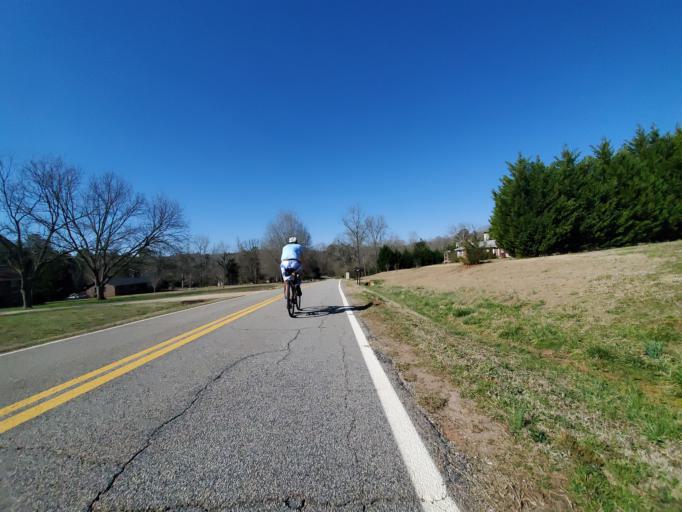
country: US
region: Georgia
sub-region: Clarke County
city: Country Club Estates
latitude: 34.0022
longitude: -83.4633
